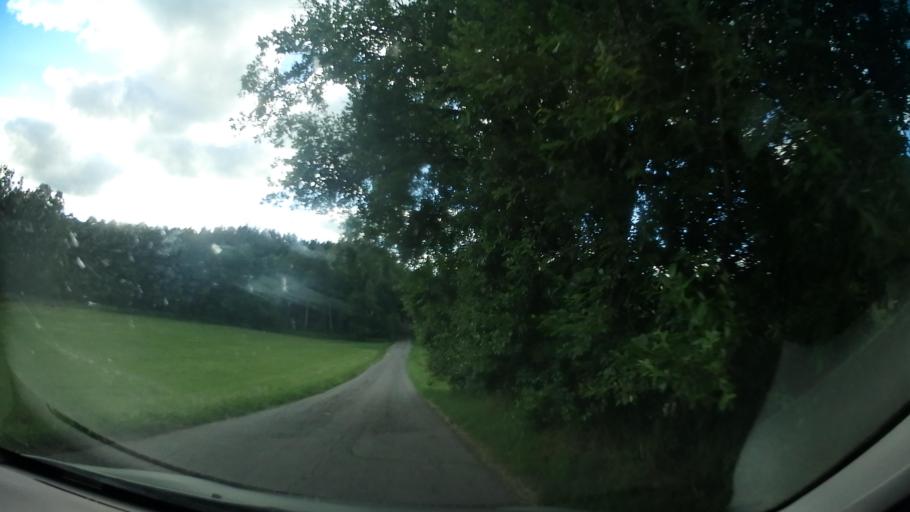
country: CZ
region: Vysocina
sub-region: Okres Zd'ar nad Sazavou
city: Jimramov
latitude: 49.6110
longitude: 16.1811
